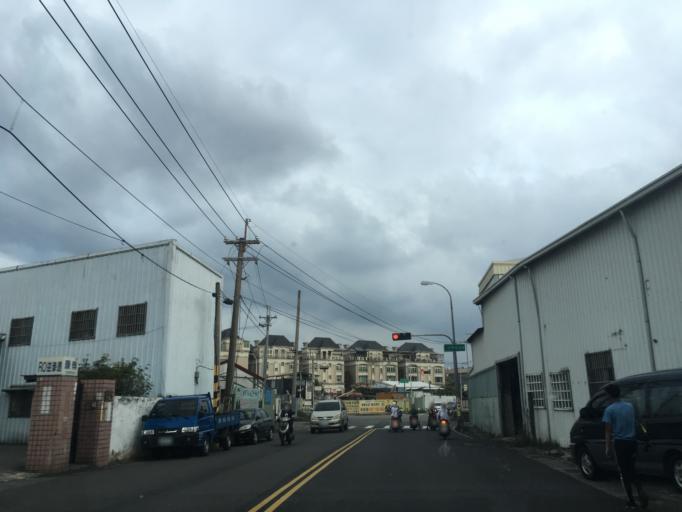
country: TW
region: Taiwan
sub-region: Taichung City
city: Taichung
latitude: 24.1694
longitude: 120.7120
